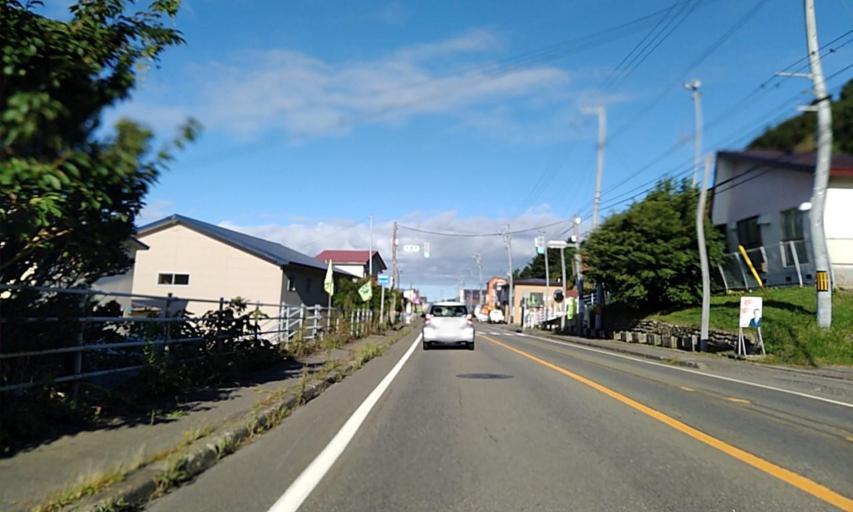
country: JP
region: Hokkaido
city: Shizunai-furukawacho
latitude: 42.1777
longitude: 142.7343
